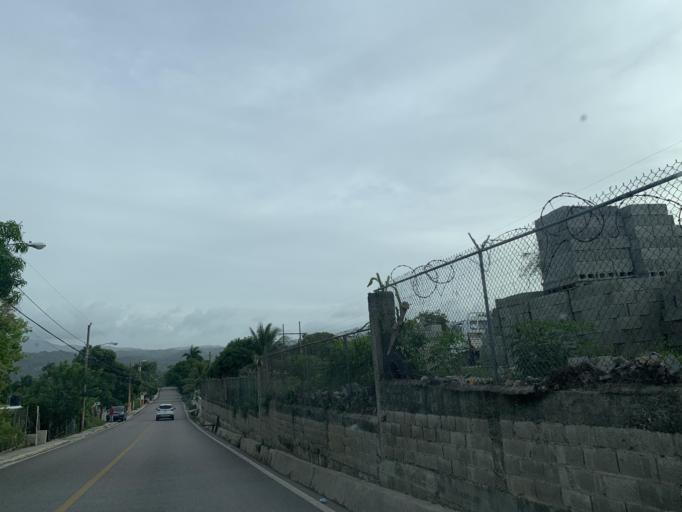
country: DO
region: Puerto Plata
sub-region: Puerto Plata
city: Puerto Plata
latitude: 19.7130
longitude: -70.6221
